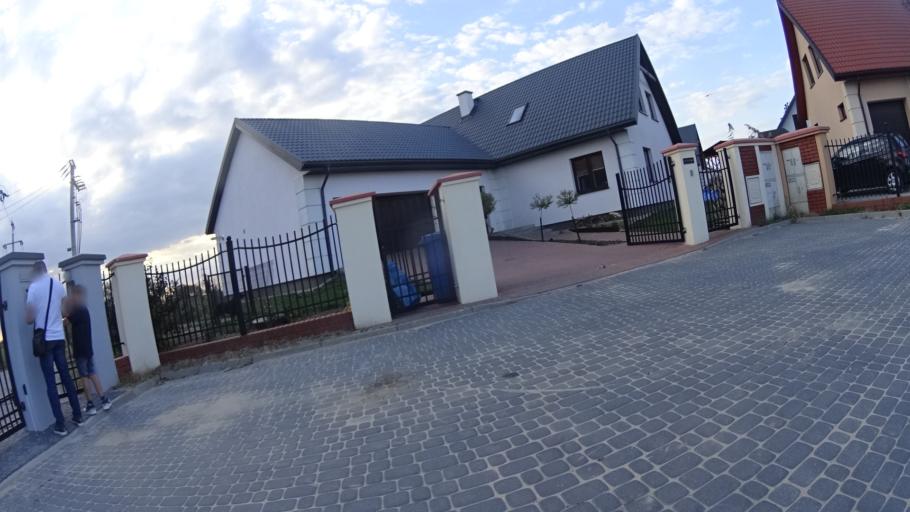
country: PL
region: Masovian Voivodeship
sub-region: Powiat warszawski zachodni
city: Ozarow Mazowiecki
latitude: 52.2330
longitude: 20.7718
